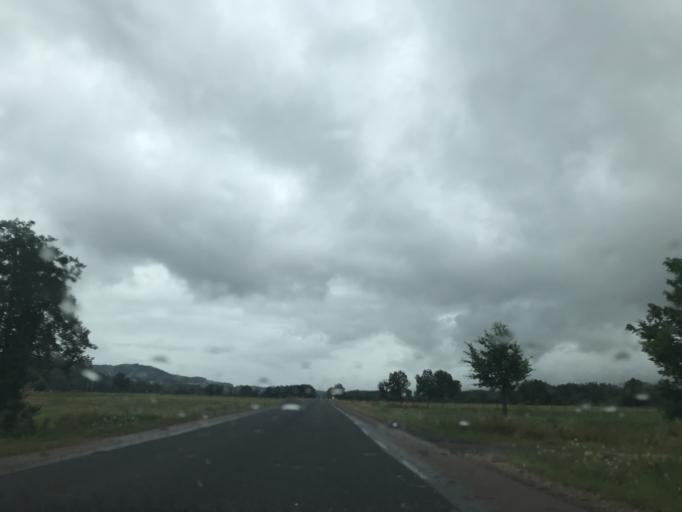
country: FR
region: Auvergne
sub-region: Departement du Puy-de-Dome
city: Marsac-en-Livradois
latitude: 45.5105
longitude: 3.7273
